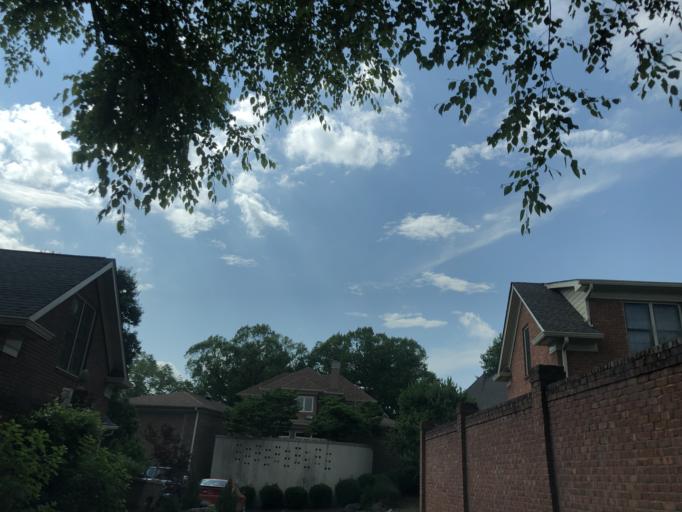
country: US
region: Tennessee
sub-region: Davidson County
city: Belle Meade
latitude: 36.1290
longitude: -86.8228
